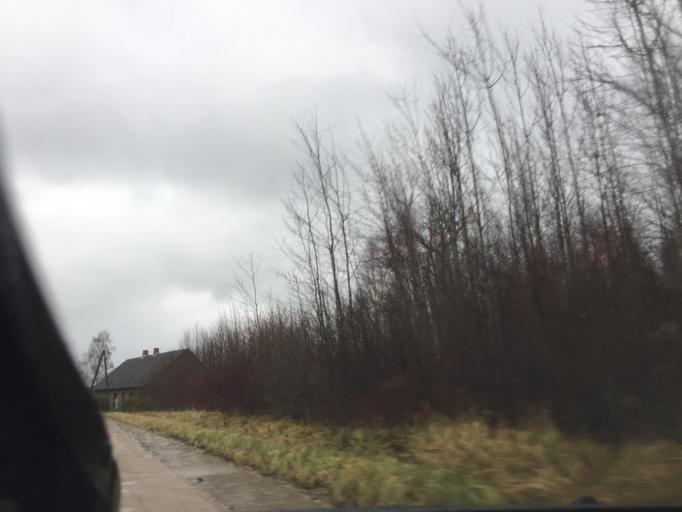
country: LV
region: Limbazu Rajons
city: Limbazi
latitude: 57.6512
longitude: 24.7771
